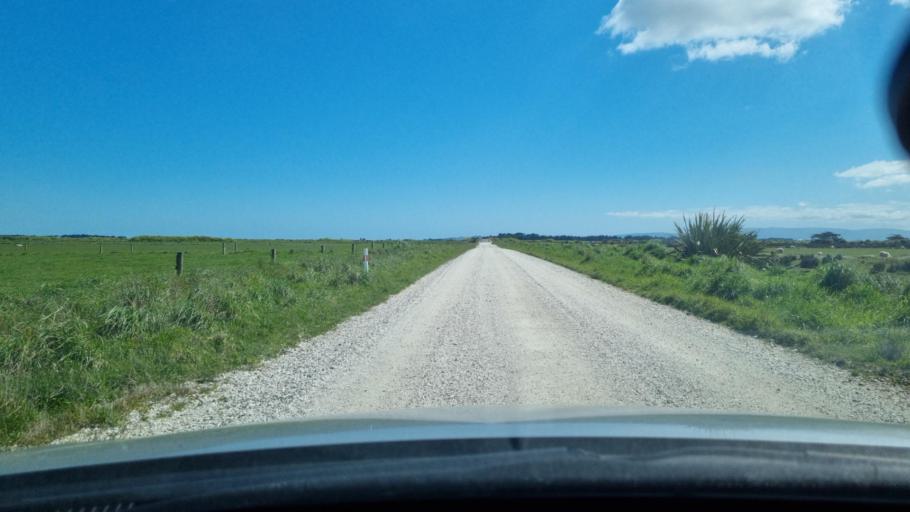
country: NZ
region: Southland
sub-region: Invercargill City
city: Invercargill
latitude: -46.3693
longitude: 168.2560
